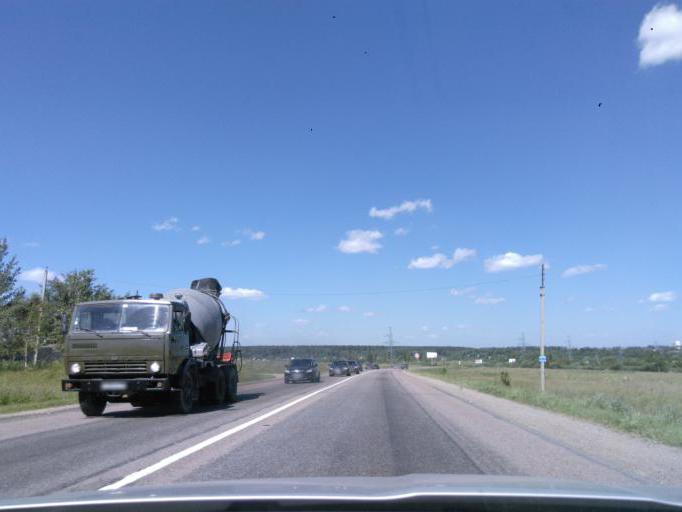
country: RU
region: Moskovskaya
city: Solnechnogorsk
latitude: 56.1637
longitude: 36.9248
